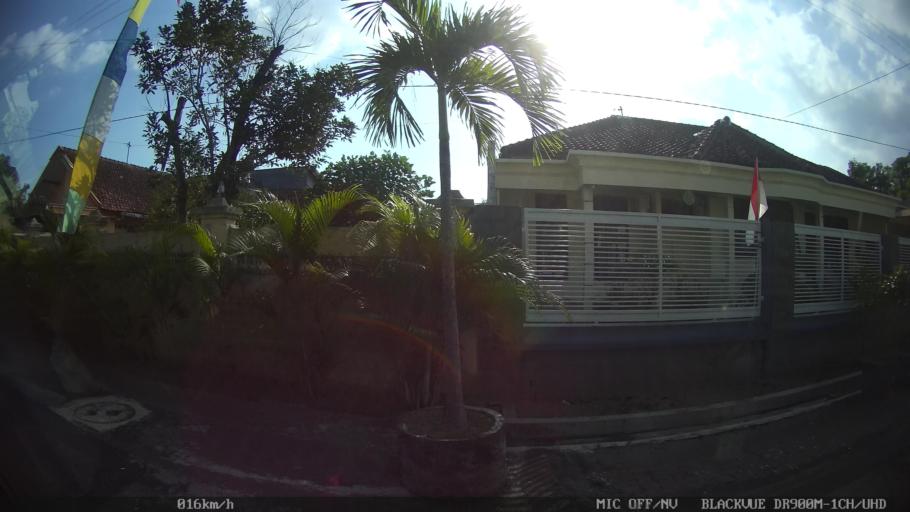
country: ID
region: Daerah Istimewa Yogyakarta
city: Yogyakarta
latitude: -7.7910
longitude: 110.3526
